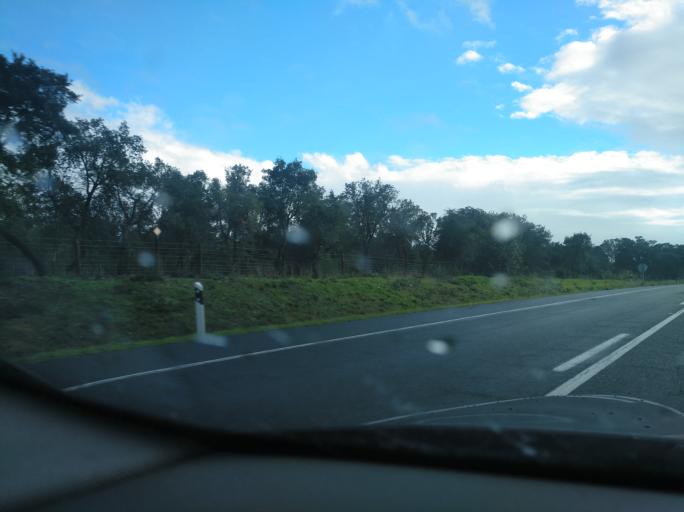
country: PT
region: Setubal
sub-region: Grandola
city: Grandola
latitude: 38.0257
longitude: -8.3996
